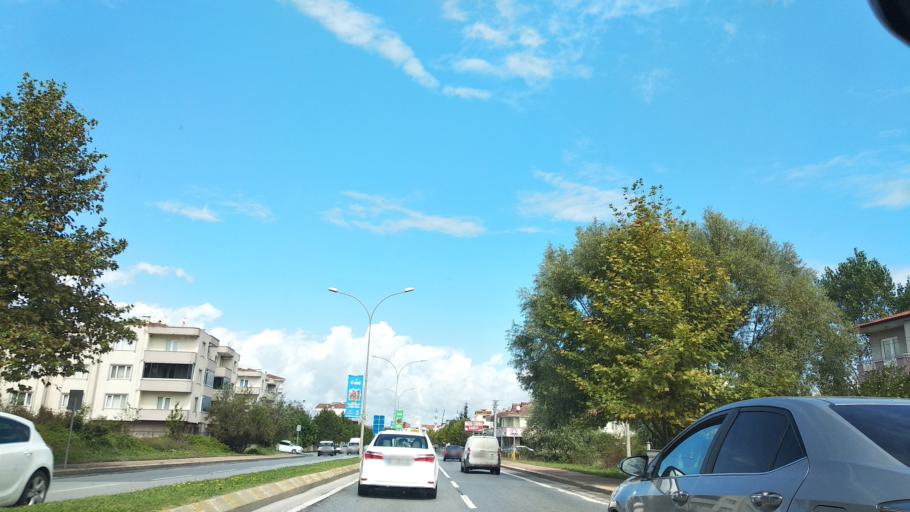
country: TR
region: Sakarya
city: Adapazari
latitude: 40.7666
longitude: 30.3638
